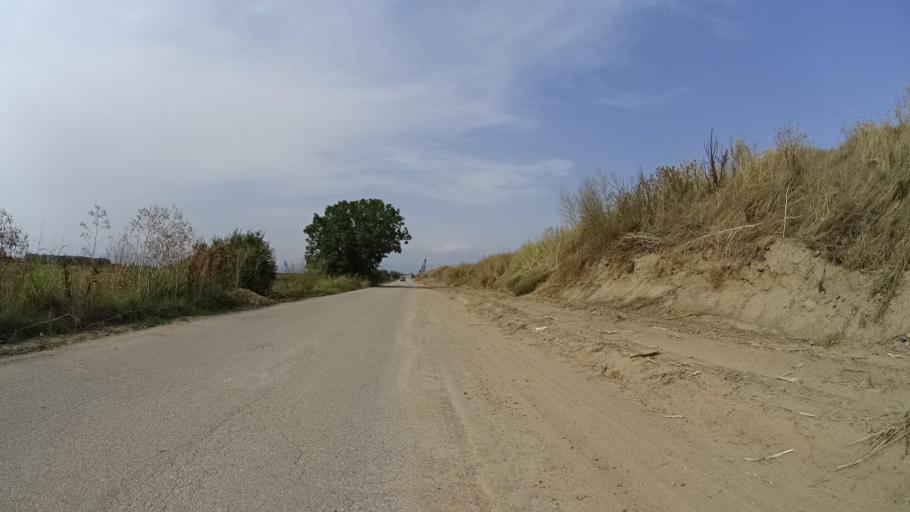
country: BG
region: Plovdiv
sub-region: Obshtina Kaloyanovo
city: Kaloyanovo
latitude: 42.3095
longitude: 24.7997
